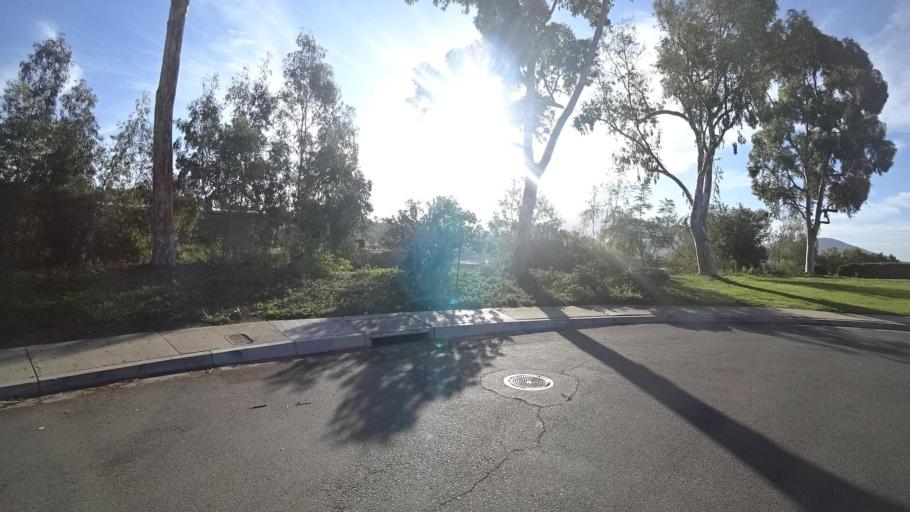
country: US
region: California
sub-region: San Diego County
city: Spring Valley
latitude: 32.7357
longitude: -116.9755
